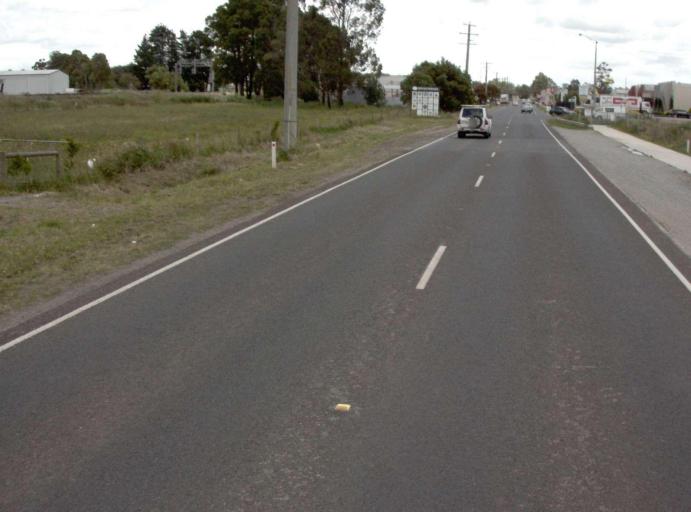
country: AU
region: Victoria
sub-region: Baw Baw
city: Warragul
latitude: -38.1672
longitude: 145.9483
